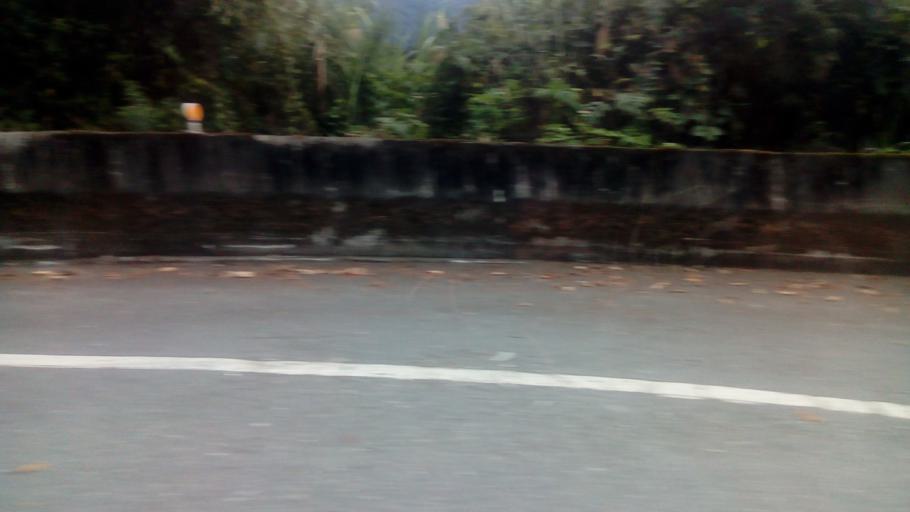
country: TW
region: Taiwan
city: Daxi
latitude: 24.4628
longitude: 121.3968
